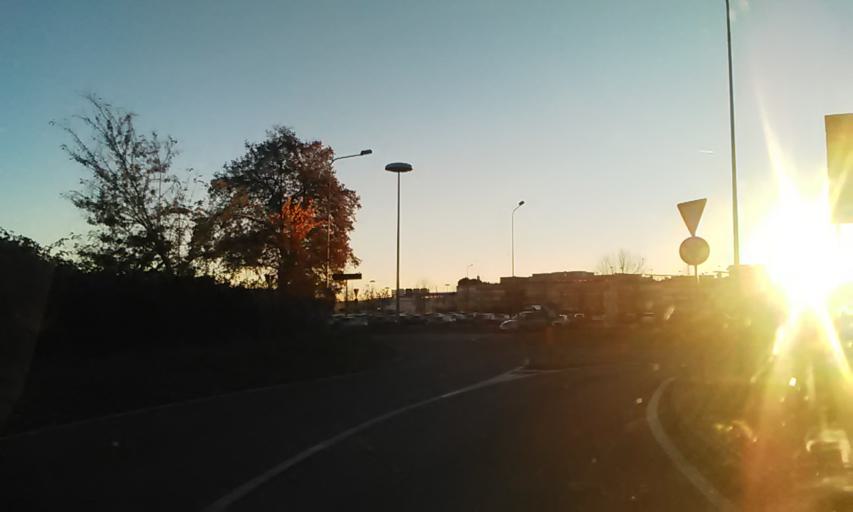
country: IT
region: Piedmont
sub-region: Provincia di Biella
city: Gaglianico
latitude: 45.5499
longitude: 8.0800
